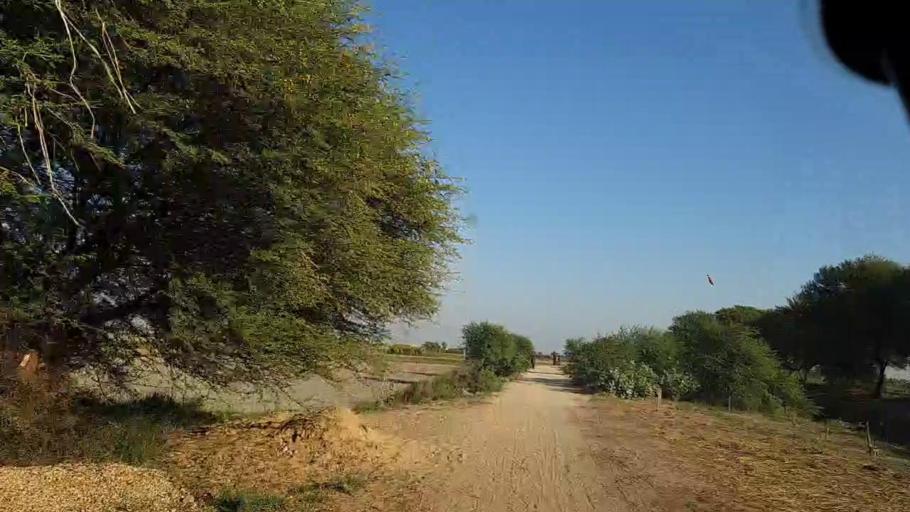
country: PK
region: Sindh
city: Chuhar Jamali
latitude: 24.5613
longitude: 68.0704
